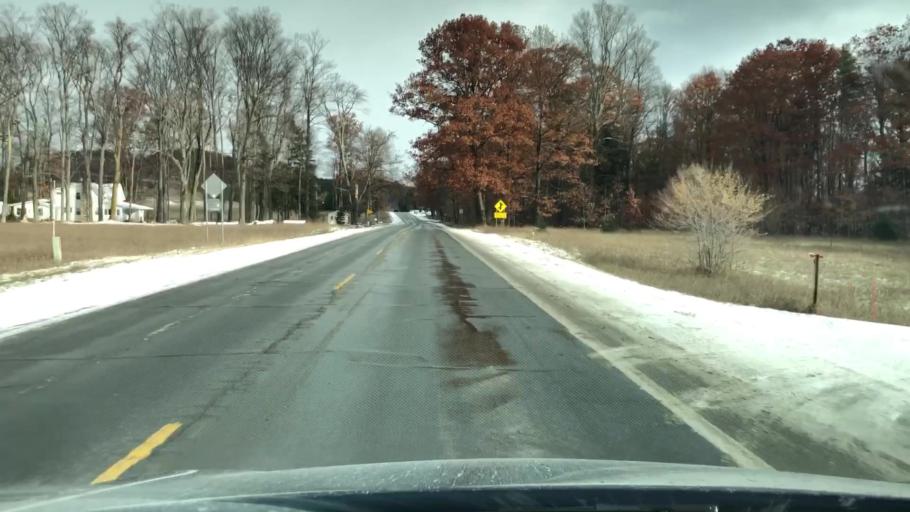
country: US
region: Michigan
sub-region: Grand Traverse County
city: Traverse City
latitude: 44.8362
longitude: -85.5381
